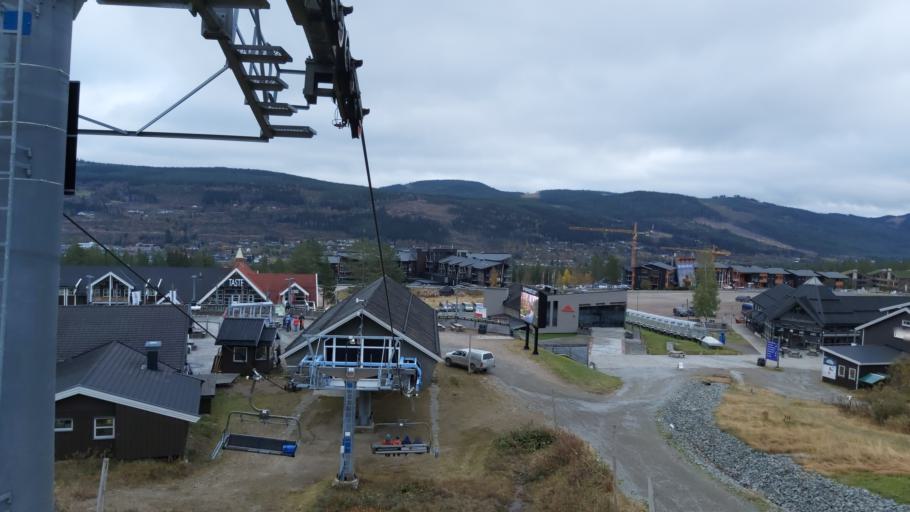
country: NO
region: Hedmark
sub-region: Trysil
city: Innbygda
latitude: 61.3079
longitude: 12.2371
